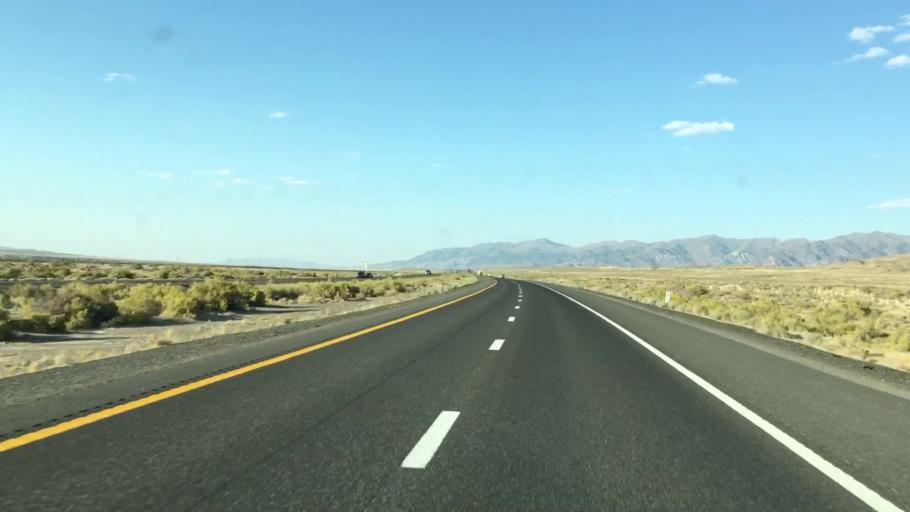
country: US
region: Nevada
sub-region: Pershing County
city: Lovelock
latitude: 40.2564
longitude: -118.3753
